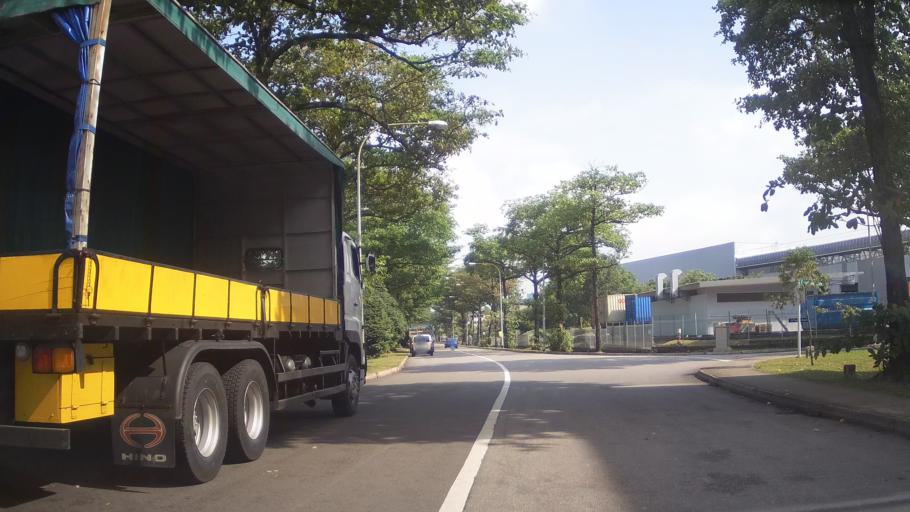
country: SG
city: Singapore
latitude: 1.3234
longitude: 103.7060
